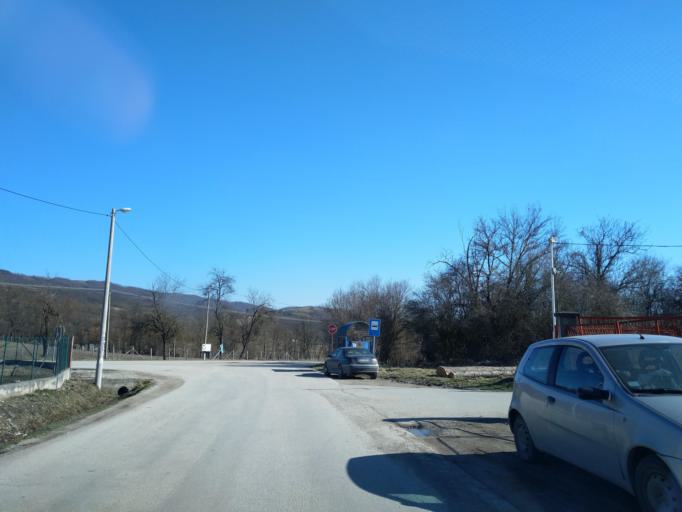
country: RS
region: Central Serbia
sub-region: Zlatiborski Okrug
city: Kosjeric
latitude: 43.9298
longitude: 19.8969
